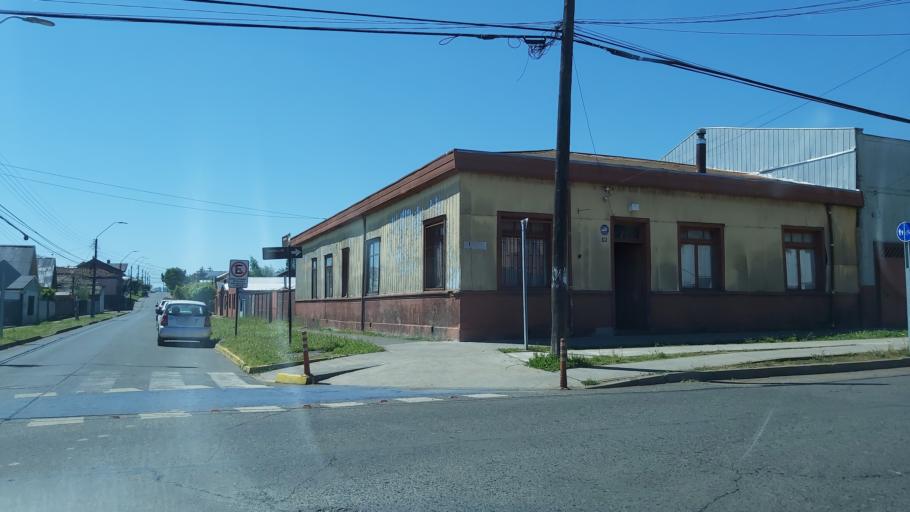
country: CL
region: Araucania
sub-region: Provincia de Malleco
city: Victoria
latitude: -38.2324
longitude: -72.3295
